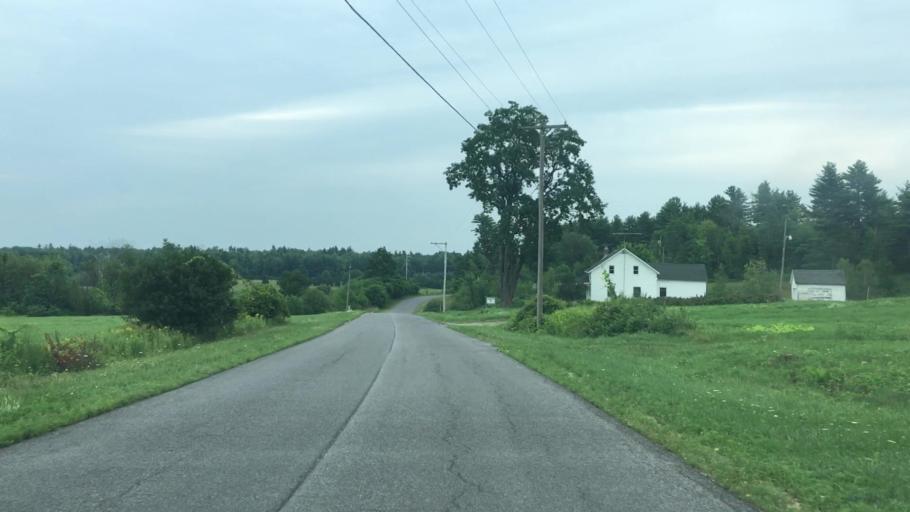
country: US
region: New York
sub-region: Clinton County
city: Peru
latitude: 44.6039
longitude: -73.6160
